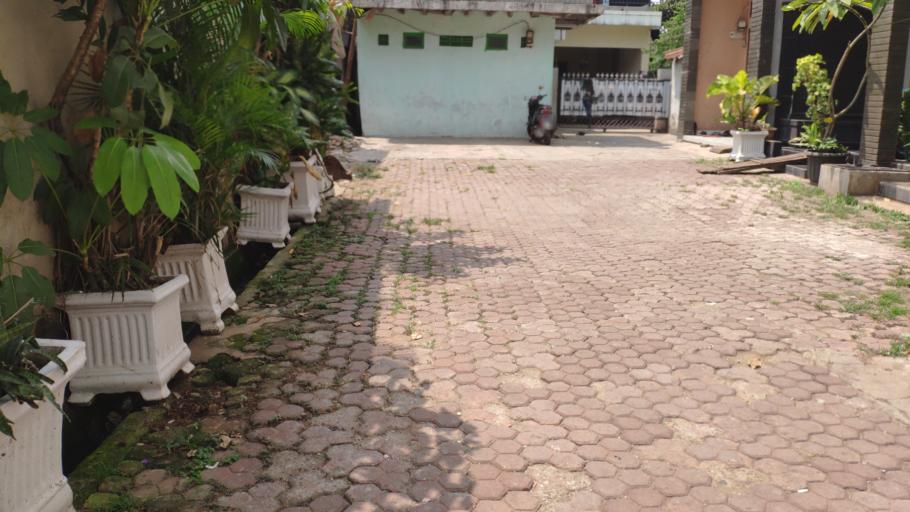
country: ID
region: Jakarta Raya
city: Jakarta
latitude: -6.2120
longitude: 106.8724
